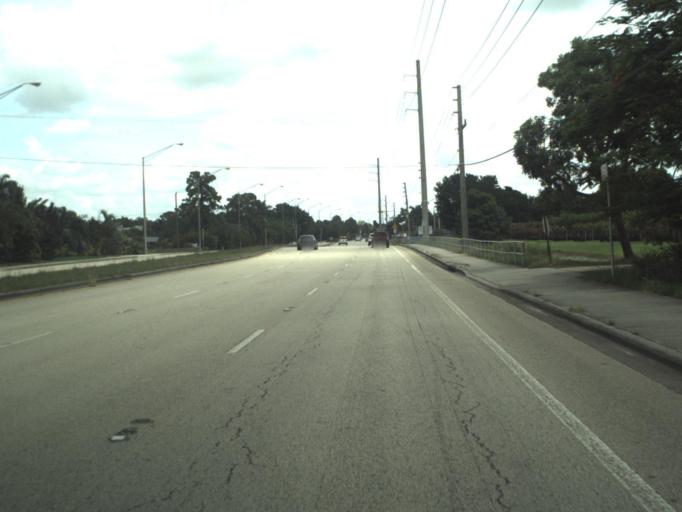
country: US
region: Florida
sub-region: Martin County
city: Palm City
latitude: 27.1662
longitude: -80.2500
